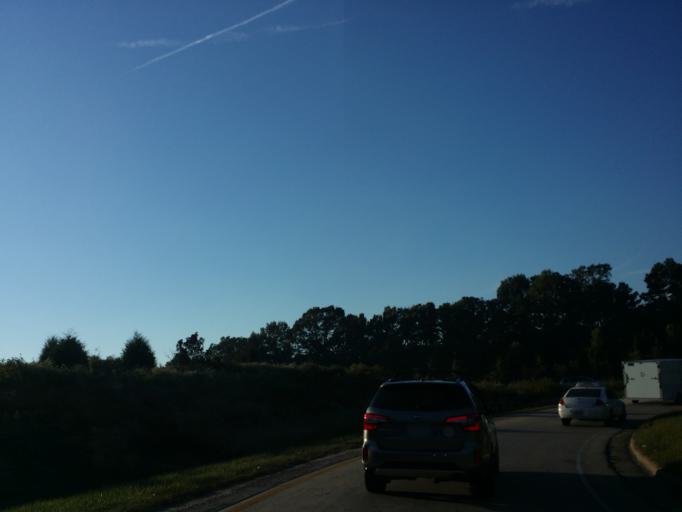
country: US
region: North Carolina
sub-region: Wake County
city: Cary
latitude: 35.7606
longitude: -78.7459
